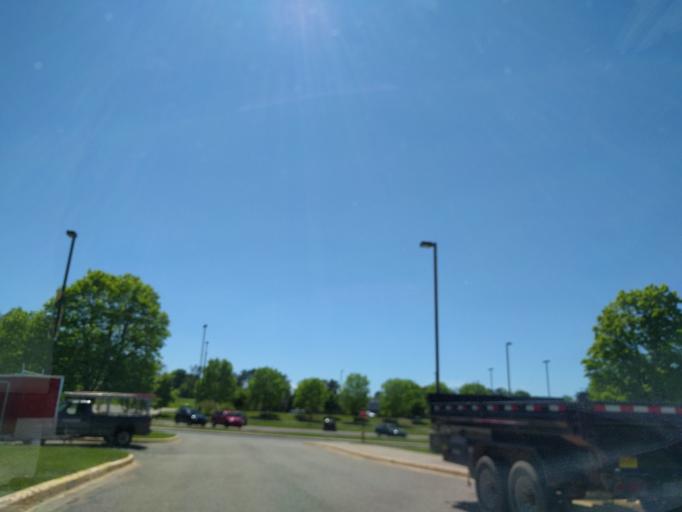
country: US
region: Michigan
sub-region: Marquette County
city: Marquette
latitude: 46.5582
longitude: -87.4078
